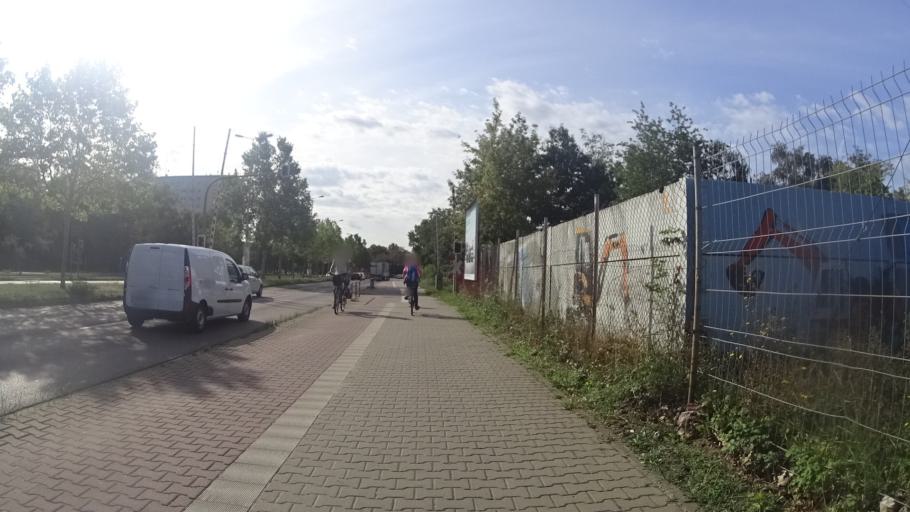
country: DE
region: Brandenburg
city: Brandenburg an der Havel
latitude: 52.4204
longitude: 12.5332
